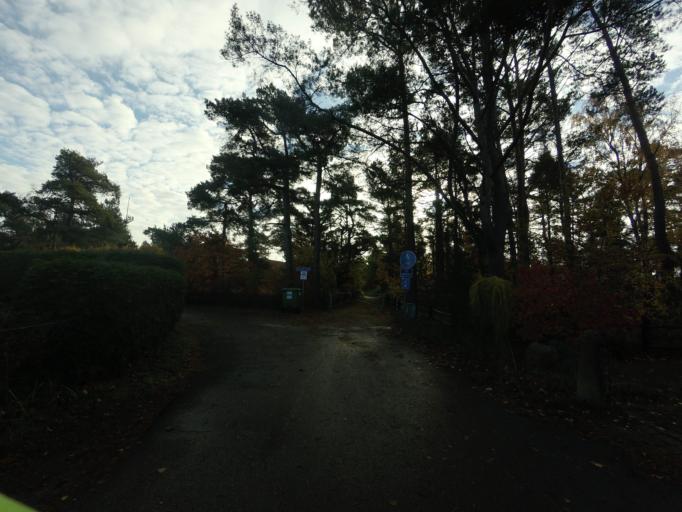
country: SE
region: Skane
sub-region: Vellinge Kommun
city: Hollviken
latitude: 55.4053
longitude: 12.9704
